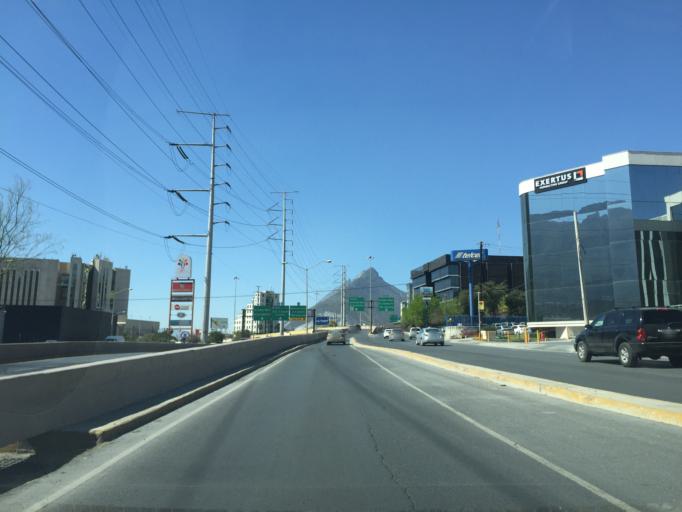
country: MX
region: Nuevo Leon
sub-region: Monterrey
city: Monterrey
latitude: 25.6528
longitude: -100.3358
